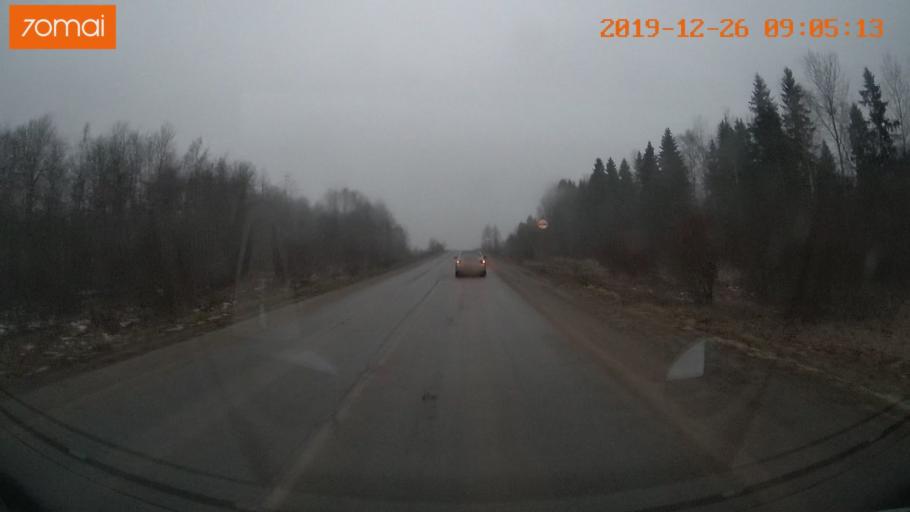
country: RU
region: Vologda
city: Gryazovets
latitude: 58.8233
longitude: 40.2590
